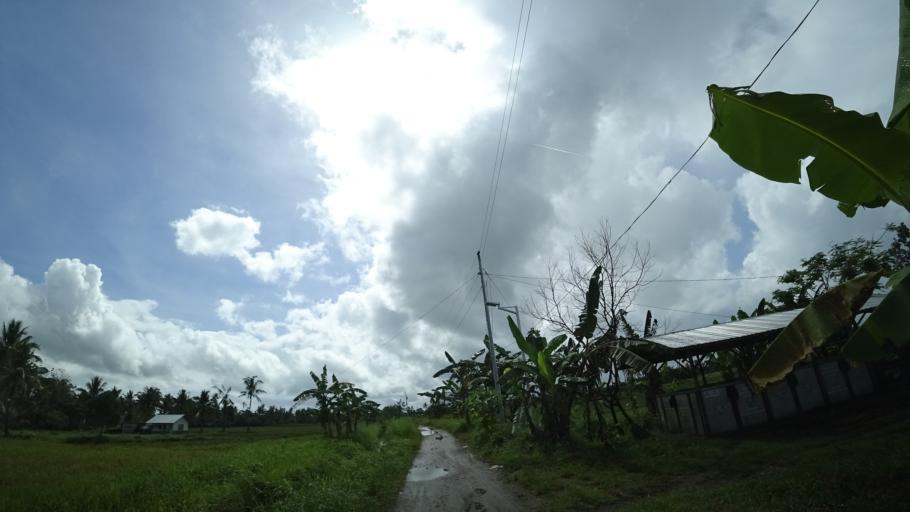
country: PH
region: Eastern Visayas
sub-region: Province of Leyte
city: Cabacungan
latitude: 10.9157
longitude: 124.9790
